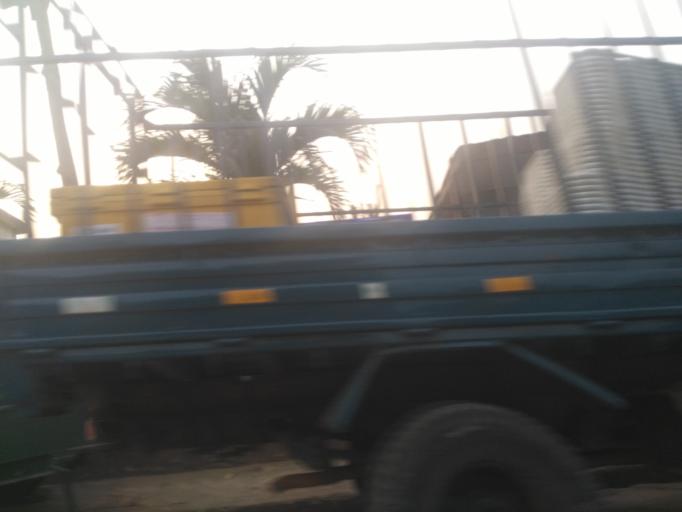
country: GH
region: Ashanti
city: Kumasi
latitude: 6.6705
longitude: -1.6032
